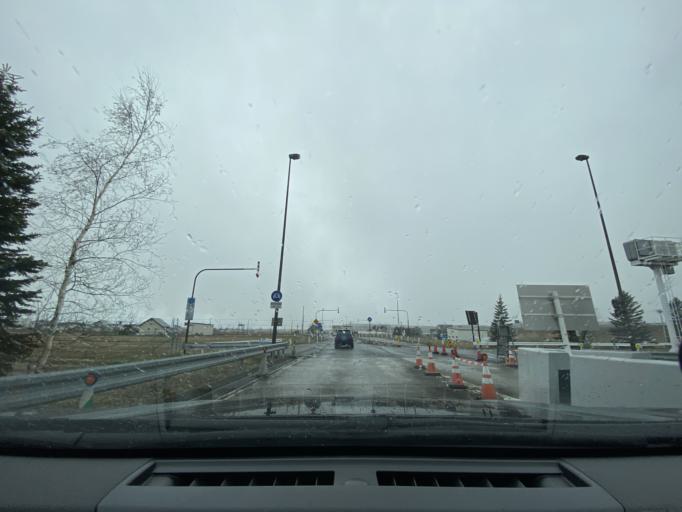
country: JP
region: Hokkaido
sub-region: Asahikawa-shi
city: Asahikawa
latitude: 43.8354
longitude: 142.4076
